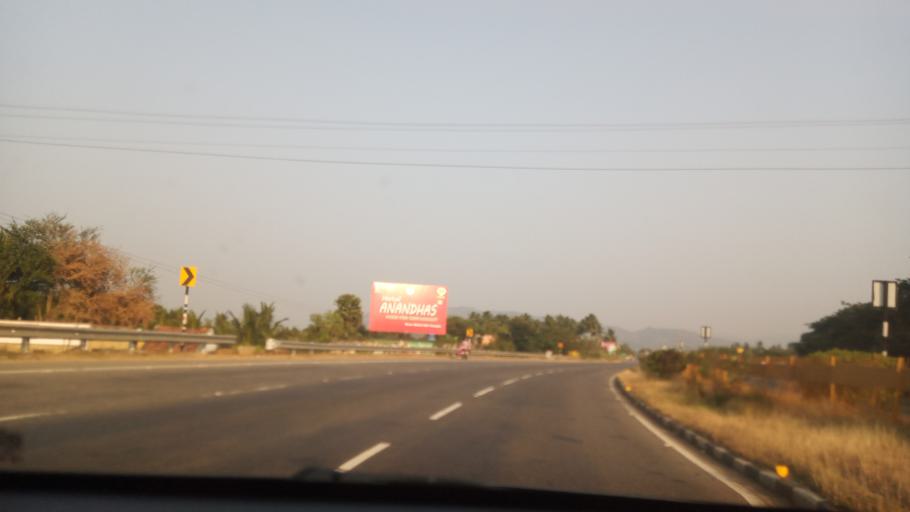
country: IN
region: Tamil Nadu
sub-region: Vellore
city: Pallikondai
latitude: 12.8917
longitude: 78.8907
